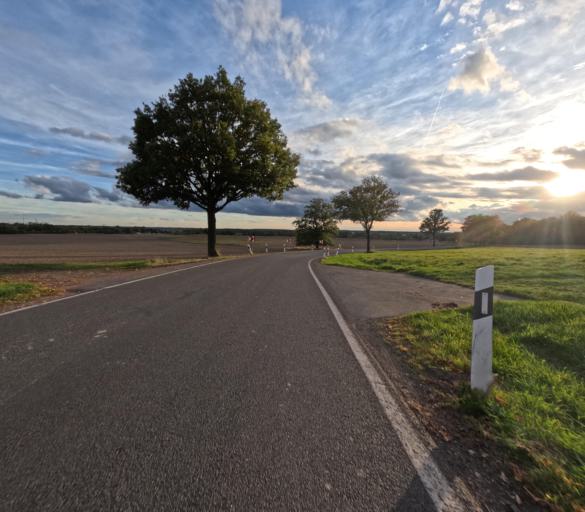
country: DE
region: Saxony
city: Grimma
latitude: 51.2488
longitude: 12.6757
